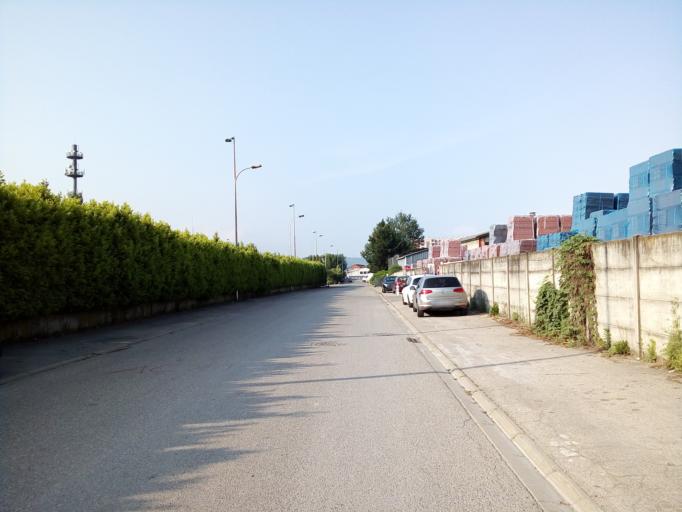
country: FR
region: Rhone-Alpes
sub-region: Departement de l'Isere
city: Saint-Martin-d'Heres
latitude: 45.1887
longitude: 5.7656
